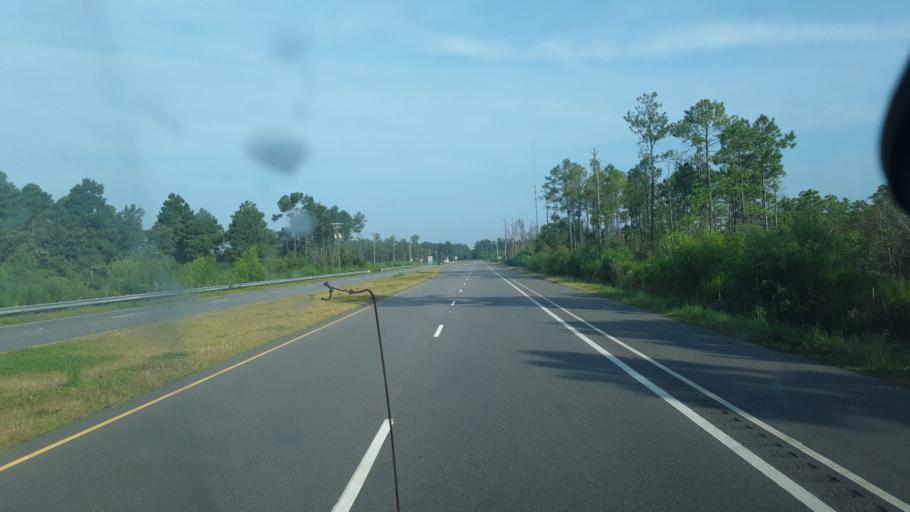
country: US
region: South Carolina
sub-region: Horry County
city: Forestbrook
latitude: 33.8126
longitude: -78.9000
